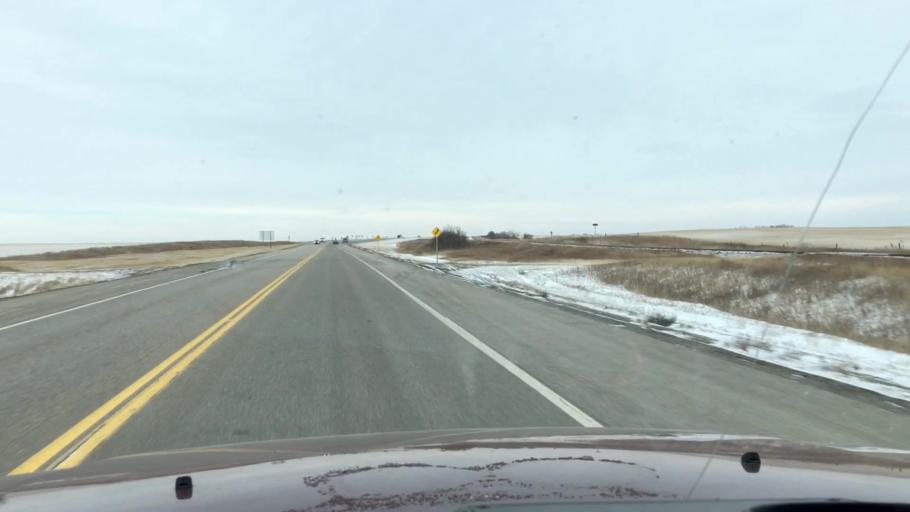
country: CA
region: Saskatchewan
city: Moose Jaw
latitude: 50.8456
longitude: -105.5565
